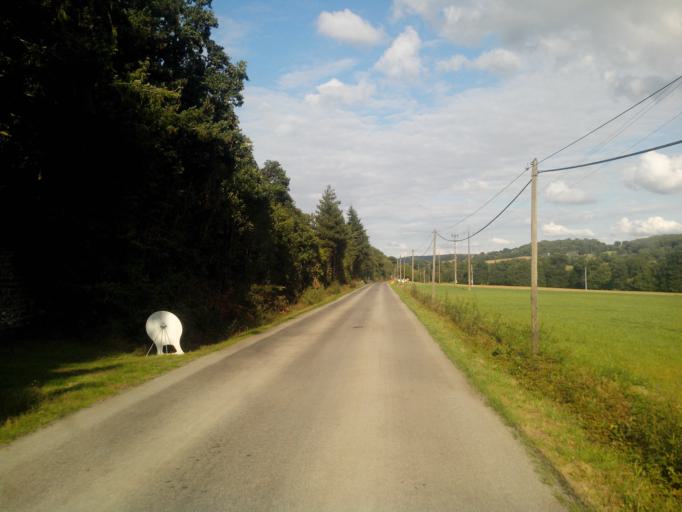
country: FR
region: Brittany
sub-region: Departement d'Ille-et-Vilaine
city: Iffendic
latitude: 48.1115
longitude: -2.0562
